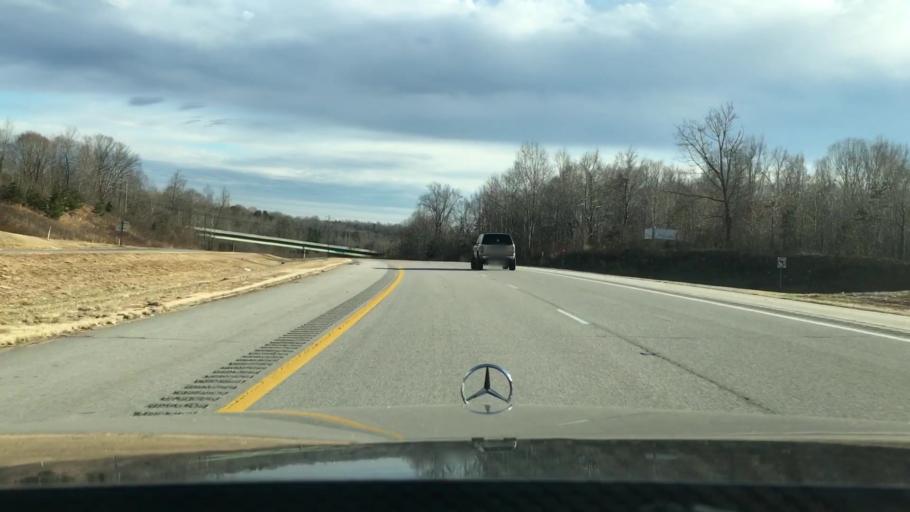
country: US
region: Virginia
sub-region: City of Danville
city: Danville
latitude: 36.6140
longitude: -79.3637
